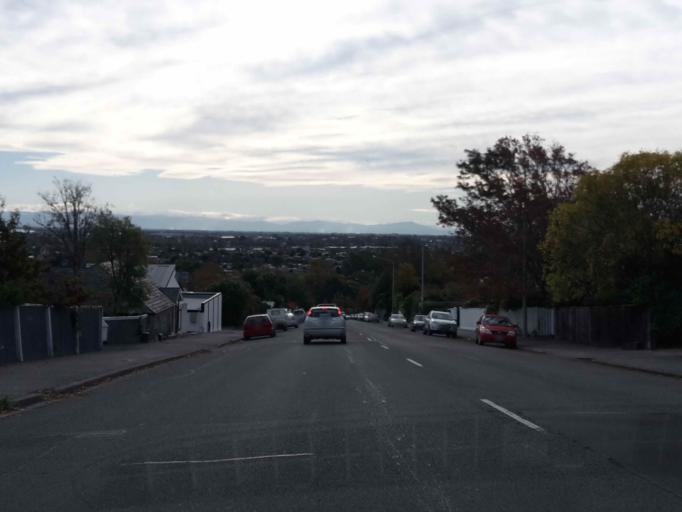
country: NZ
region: Canterbury
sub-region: Christchurch City
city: Christchurch
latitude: -43.5728
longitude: 172.6246
